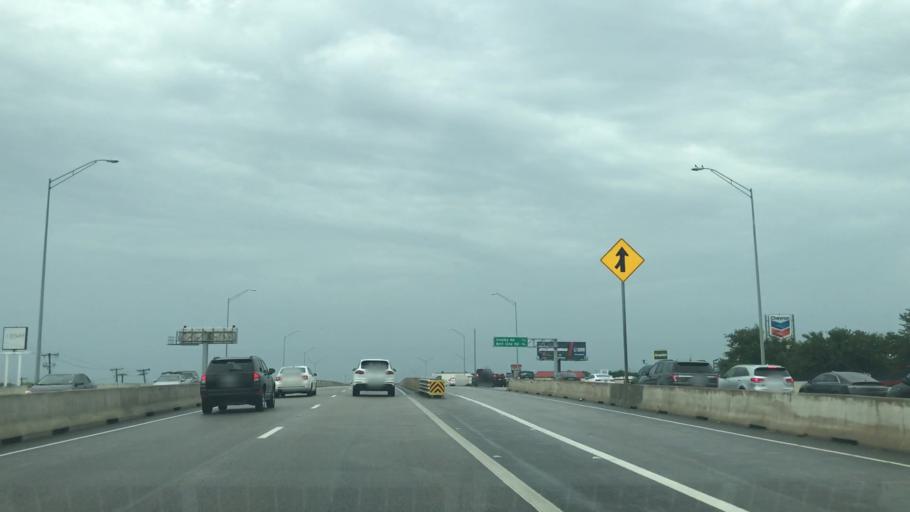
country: US
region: Texas
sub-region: Dallas County
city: Carrollton
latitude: 32.9529
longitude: -96.9034
